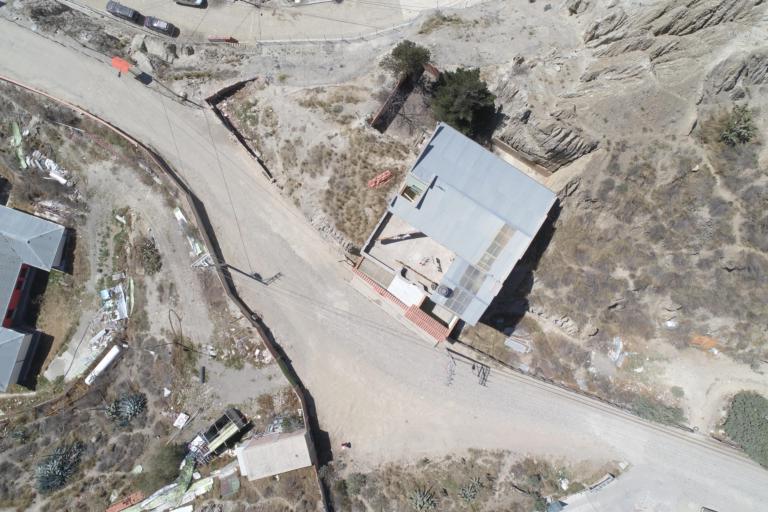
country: BO
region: La Paz
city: La Paz
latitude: -16.5178
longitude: -68.1252
